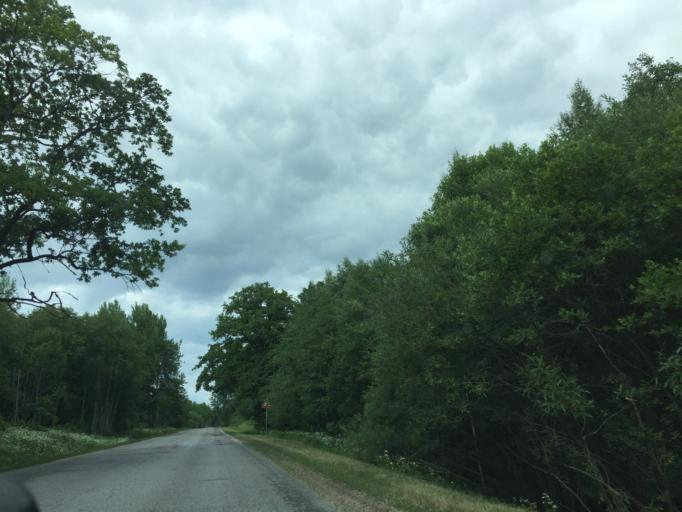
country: LV
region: Skriveri
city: Skriveri
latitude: 56.8285
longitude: 25.1265
